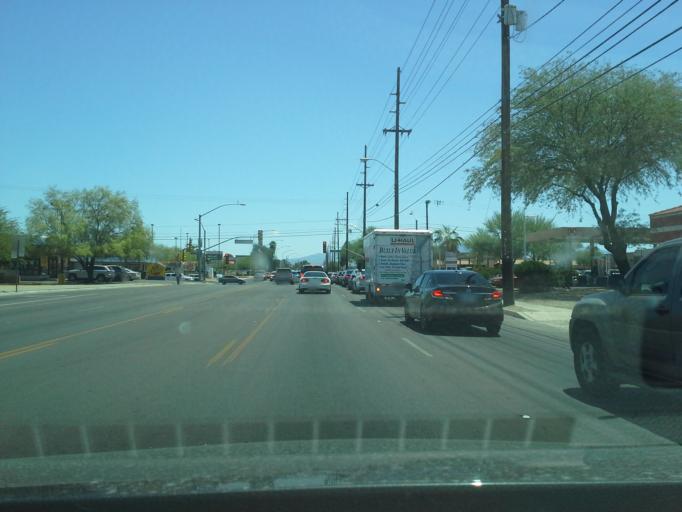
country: US
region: Arizona
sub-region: Pima County
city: Tucson
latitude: 32.2506
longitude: -110.9109
